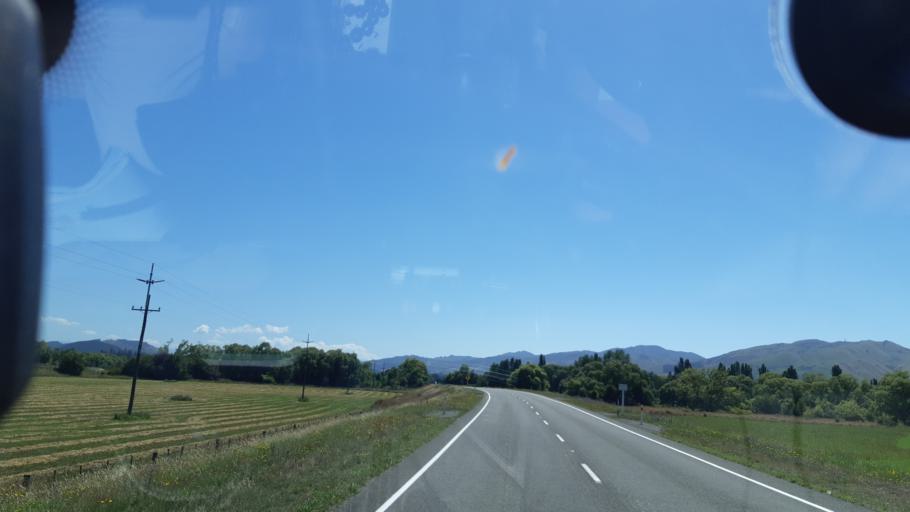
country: NZ
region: Canterbury
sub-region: Kaikoura District
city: Kaikoura
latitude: -42.7276
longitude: 173.2783
